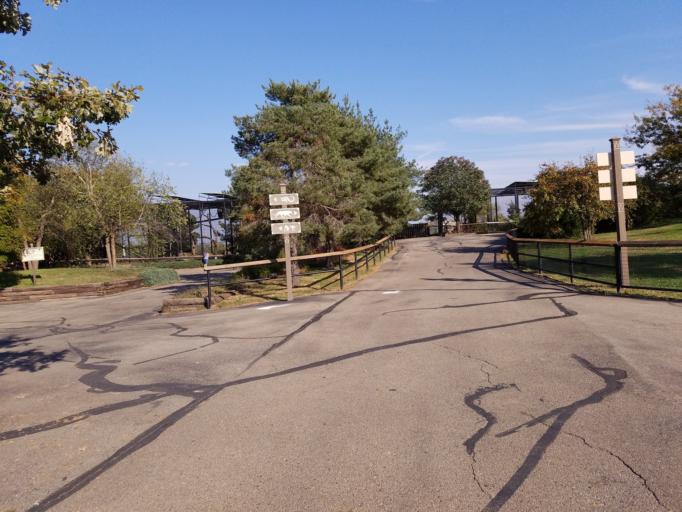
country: US
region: Kansas
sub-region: Saline County
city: Salina
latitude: 38.8539
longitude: -97.7627
